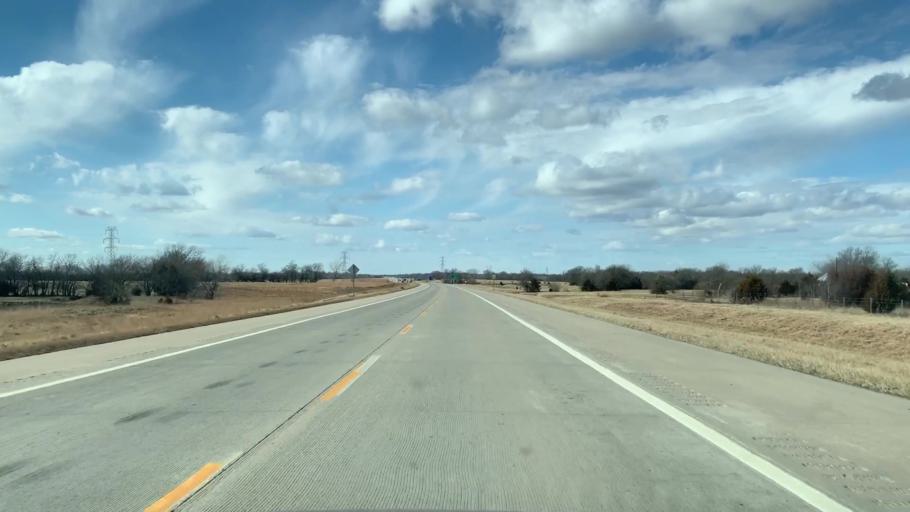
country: US
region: Kansas
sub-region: Labette County
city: Parsons
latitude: 37.3625
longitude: -95.2333
